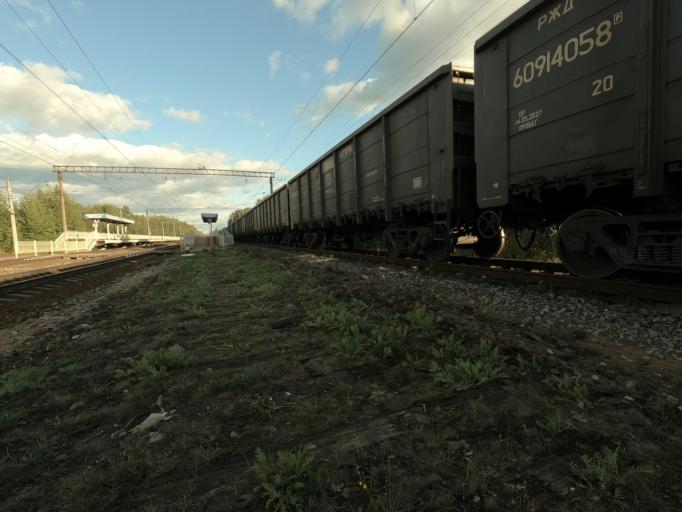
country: RU
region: Leningrad
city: Imeni Sverdlova
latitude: 59.8548
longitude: 30.7305
